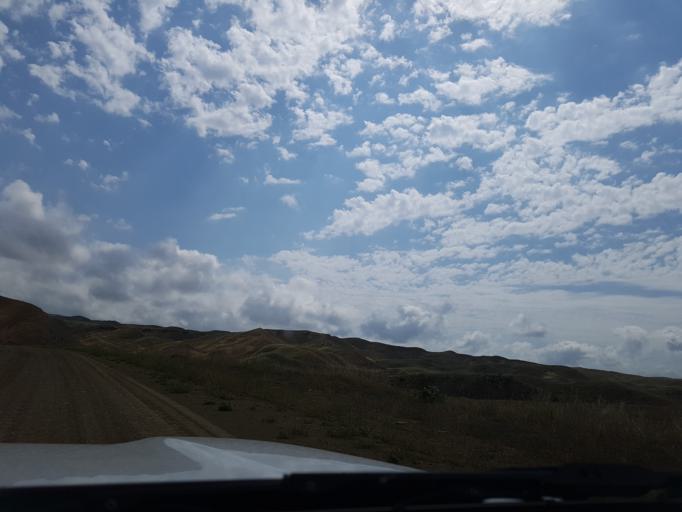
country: TM
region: Balkan
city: Magtymguly
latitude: 38.2649
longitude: 56.7884
